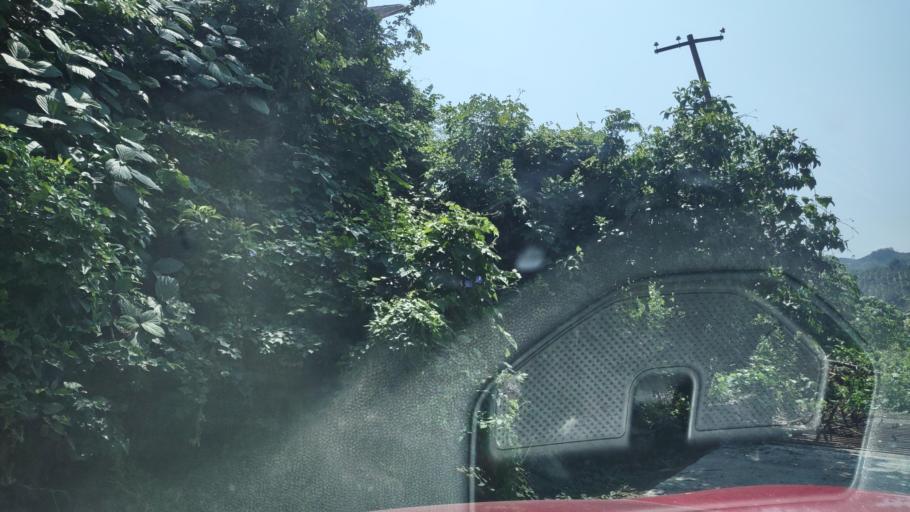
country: MX
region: Veracruz
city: Agua Dulce
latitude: 20.3093
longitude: -97.1704
